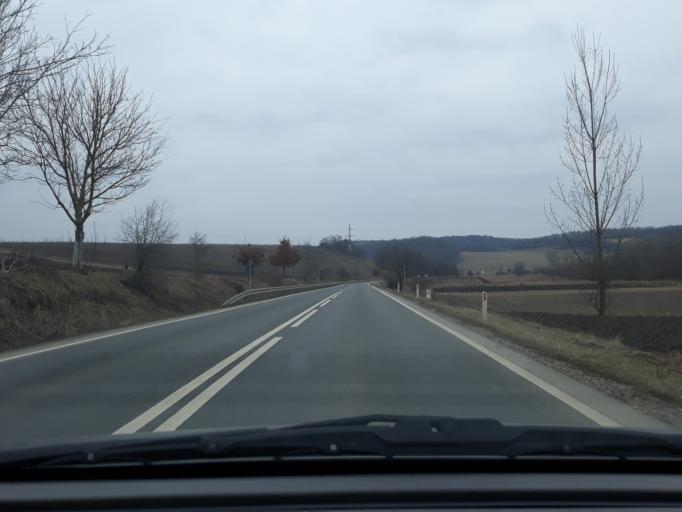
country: RO
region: Salaj
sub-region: Comuna Nusfalau
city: Nusfalau
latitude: 47.2208
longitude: 22.7366
